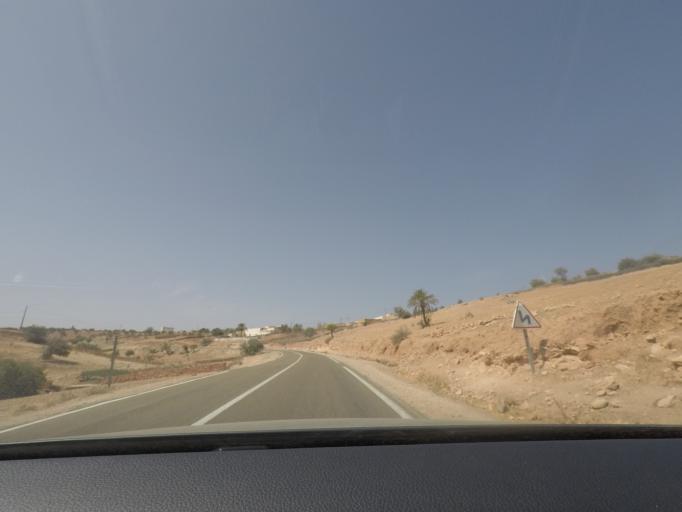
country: MA
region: Marrakech-Tensift-Al Haouz
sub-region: Essaouira
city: Tamanar
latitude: 31.0835
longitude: -9.6647
